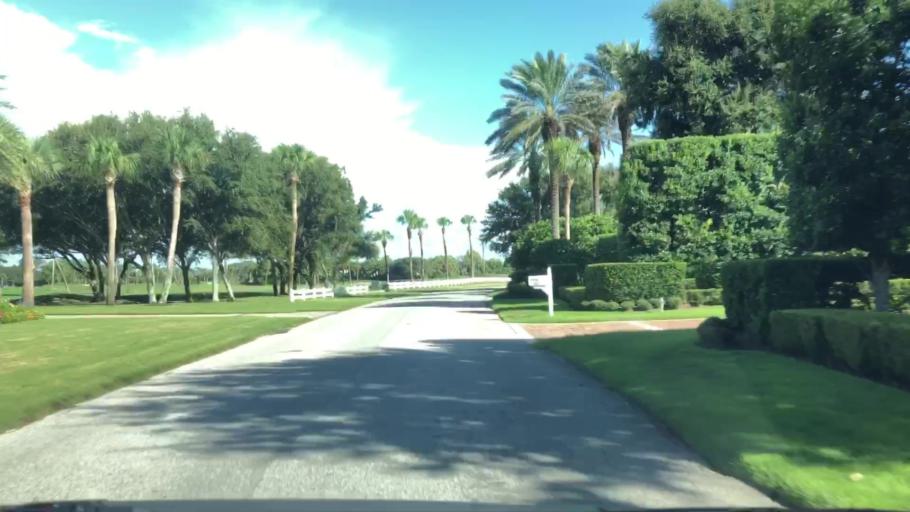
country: US
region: Florida
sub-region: Saint Johns County
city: Ponte Vedra Beach
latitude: 30.2356
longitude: -81.3802
